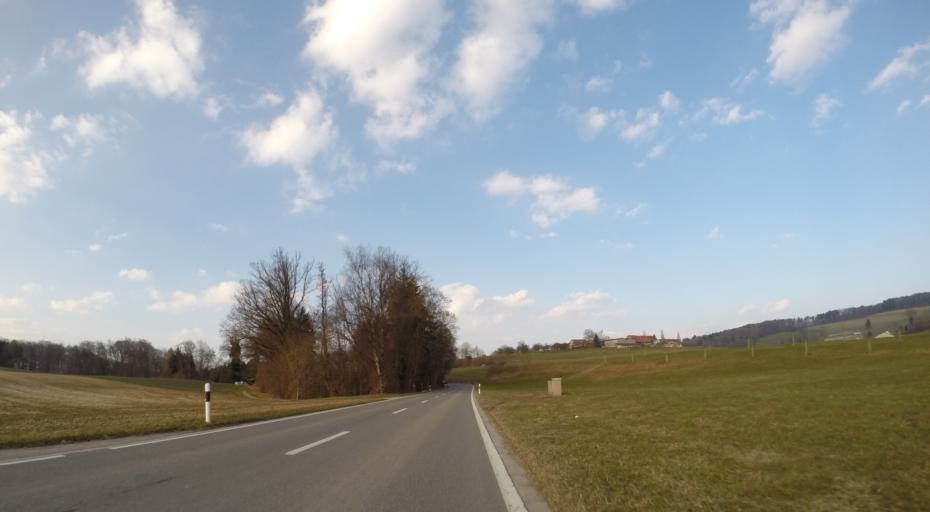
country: CH
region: Thurgau
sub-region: Frauenfeld District
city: Steckborn
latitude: 47.6454
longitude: 8.9788
